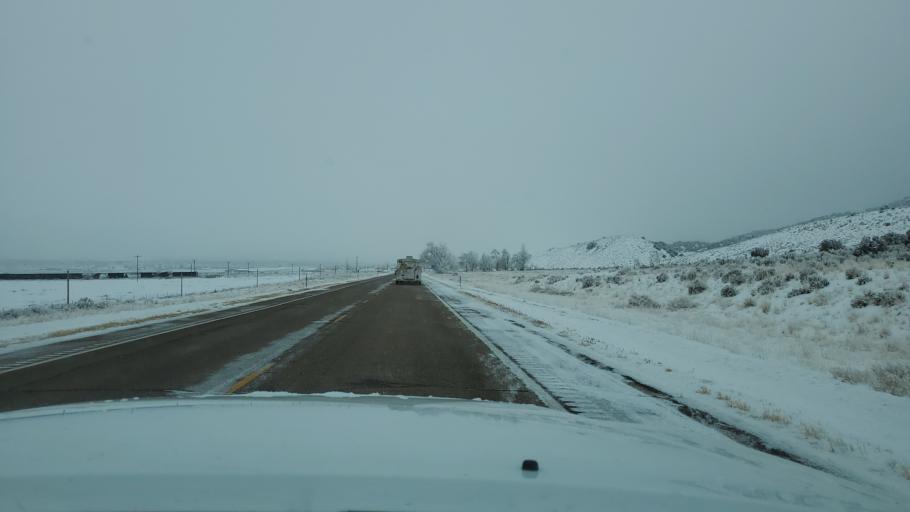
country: US
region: Colorado
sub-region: Rio Blanco County
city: Rangely
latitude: 40.2434
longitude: -108.9885
